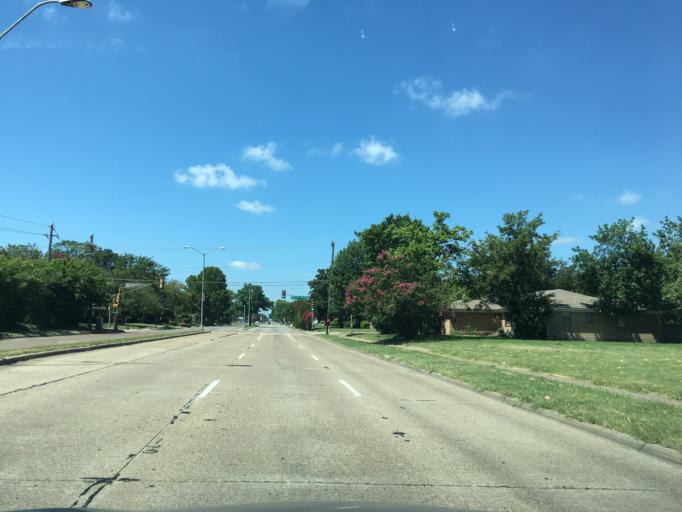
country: US
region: Texas
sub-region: Dallas County
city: Garland
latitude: 32.8477
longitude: -96.6587
